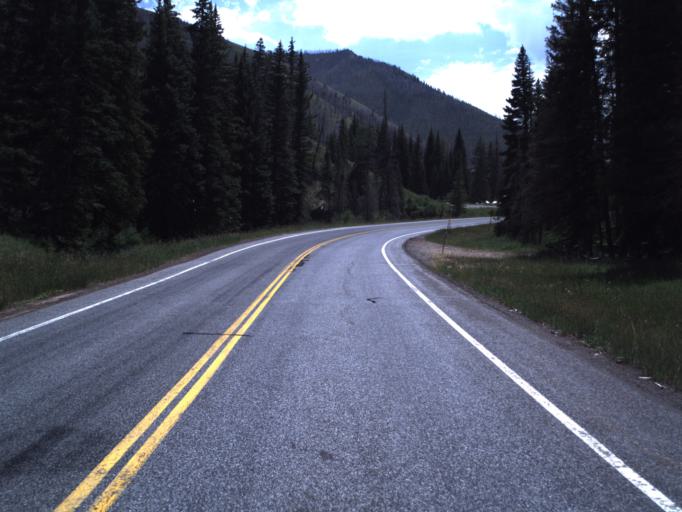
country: US
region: Utah
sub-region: Emery County
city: Huntington
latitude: 39.5326
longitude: -111.1554
